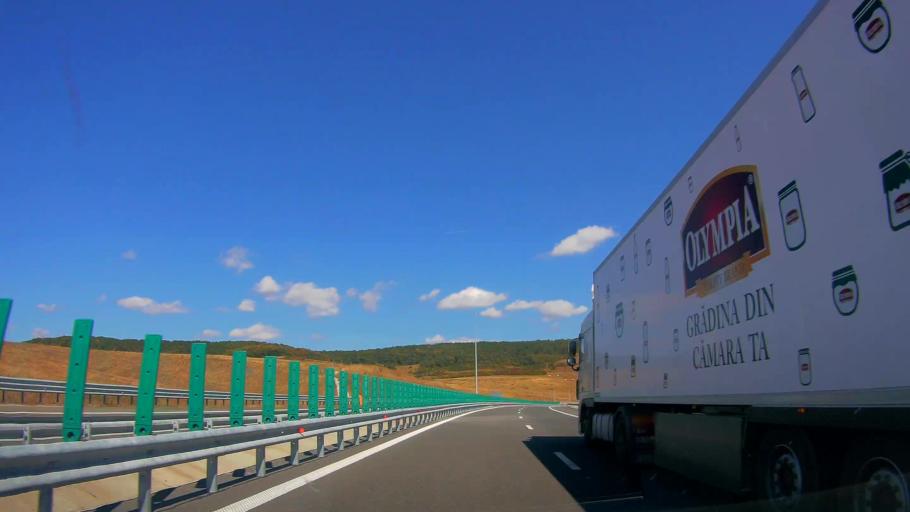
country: RO
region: Cluj
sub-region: Comuna Gilau
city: Gilau
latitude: 46.7732
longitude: 23.3846
